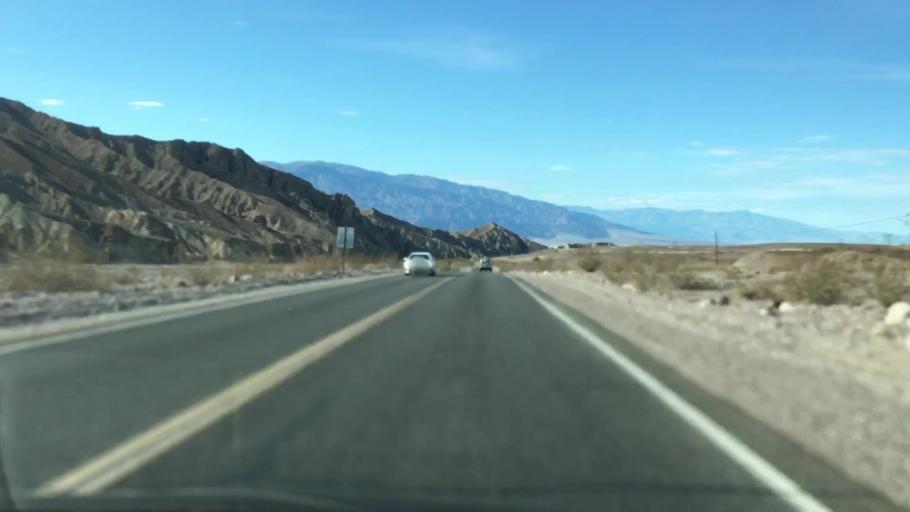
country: US
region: Nevada
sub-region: Nye County
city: Beatty
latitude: 36.4374
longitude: -116.8236
